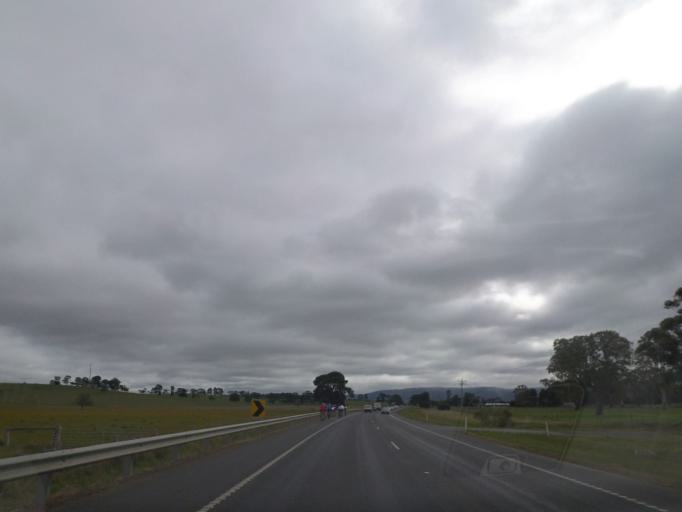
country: AU
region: Victoria
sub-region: Whittlesea
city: Whittlesea
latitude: -37.5484
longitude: 145.1090
